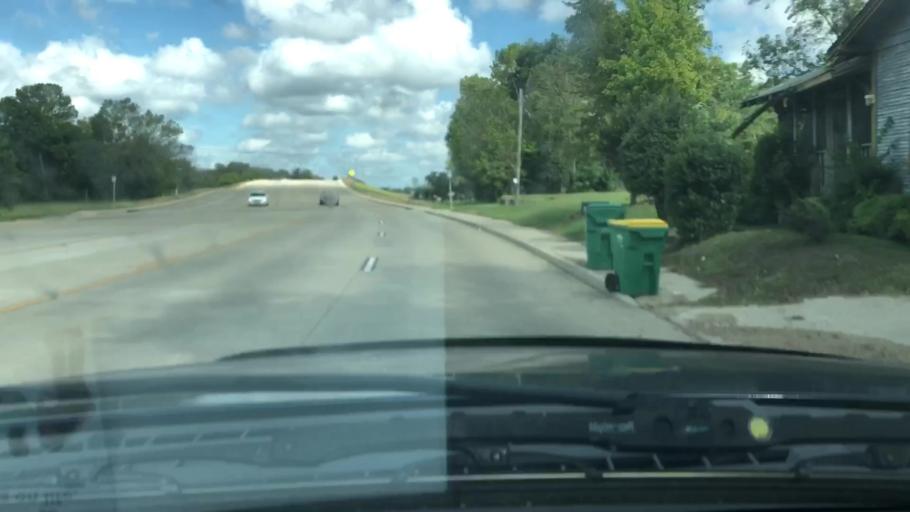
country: US
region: Texas
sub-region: Bowie County
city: Texarkana
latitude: 33.4105
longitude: -94.0605
